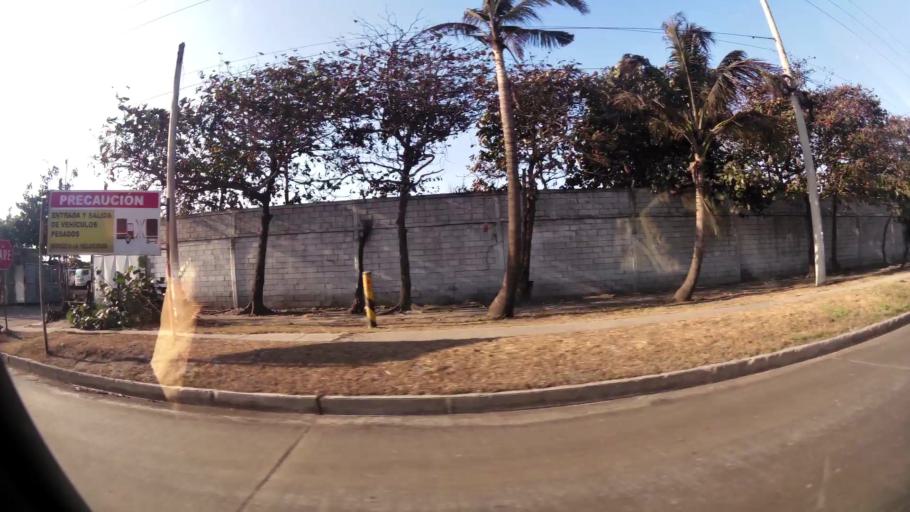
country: CO
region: Atlantico
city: Barranquilla
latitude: 11.0372
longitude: -74.8170
